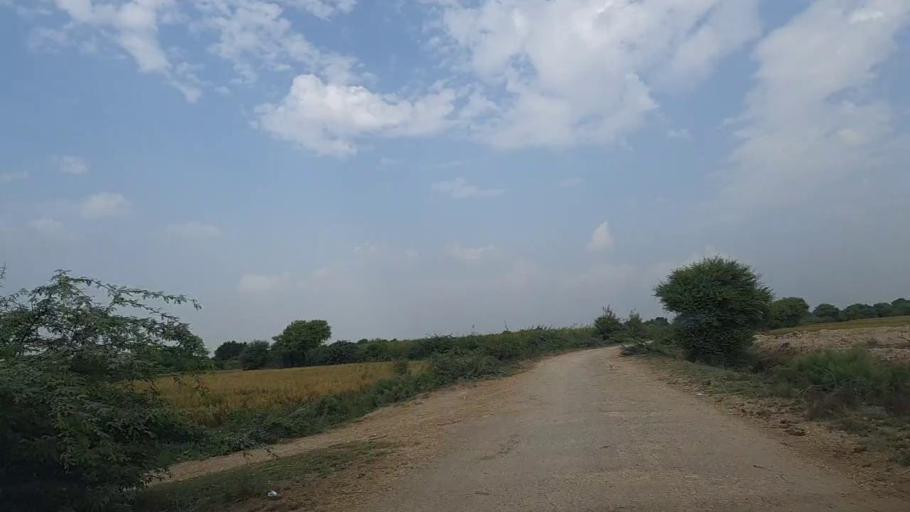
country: PK
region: Sindh
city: Daro Mehar
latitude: 24.7127
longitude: 68.1531
